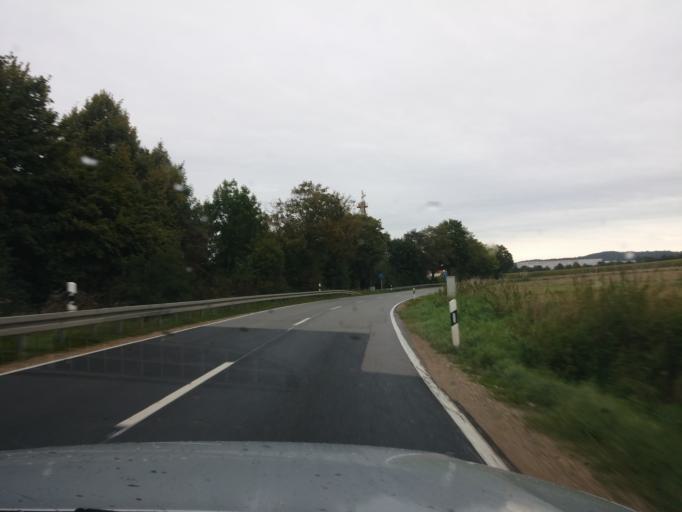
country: DE
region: Bavaria
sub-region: Upper Bavaria
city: Allershausen
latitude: 48.4275
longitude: 11.5700
